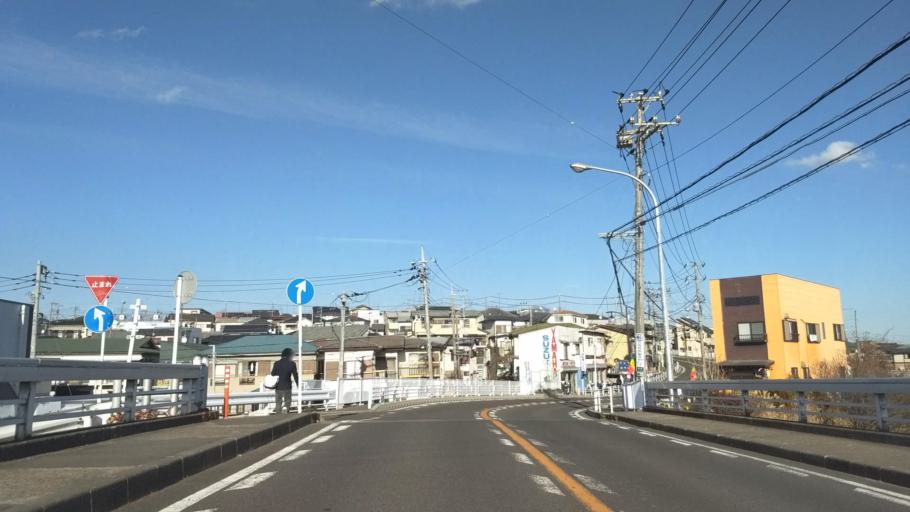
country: JP
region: Kanagawa
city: Isehara
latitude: 35.3731
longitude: 139.2749
